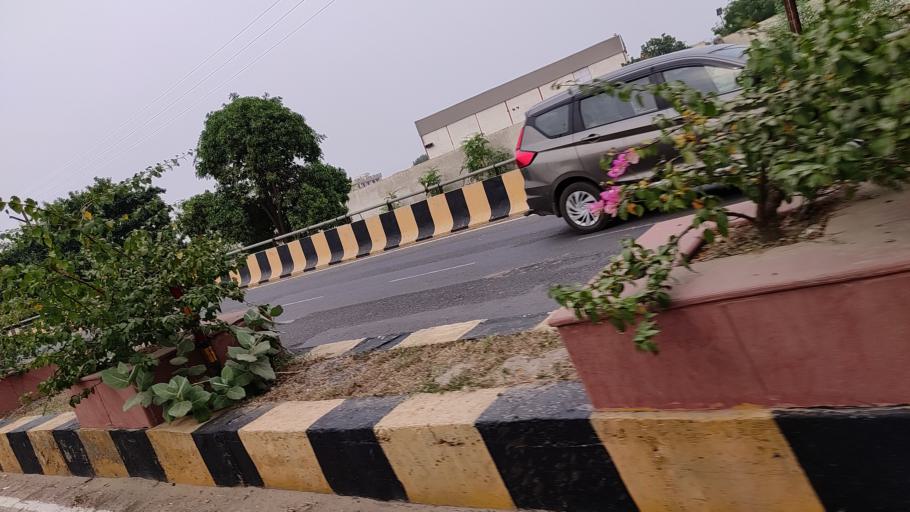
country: IN
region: Uttar Pradesh
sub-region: Mathura
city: Vrindavan
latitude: 27.5621
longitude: 77.6818
